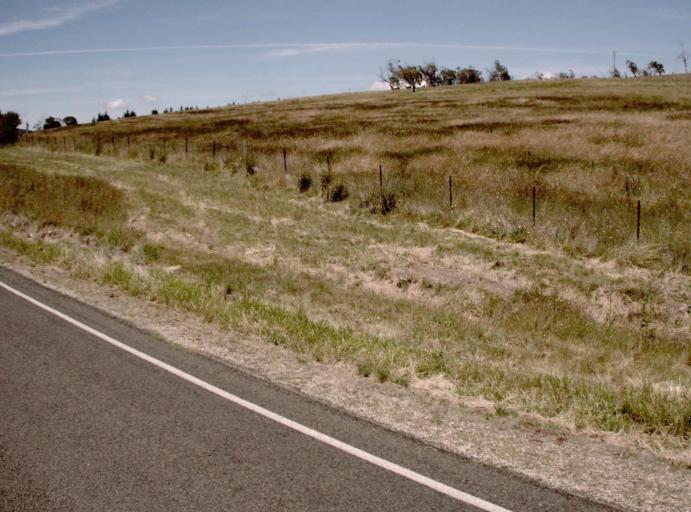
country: AU
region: Victoria
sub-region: Alpine
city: Mount Beauty
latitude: -37.1326
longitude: 147.6451
